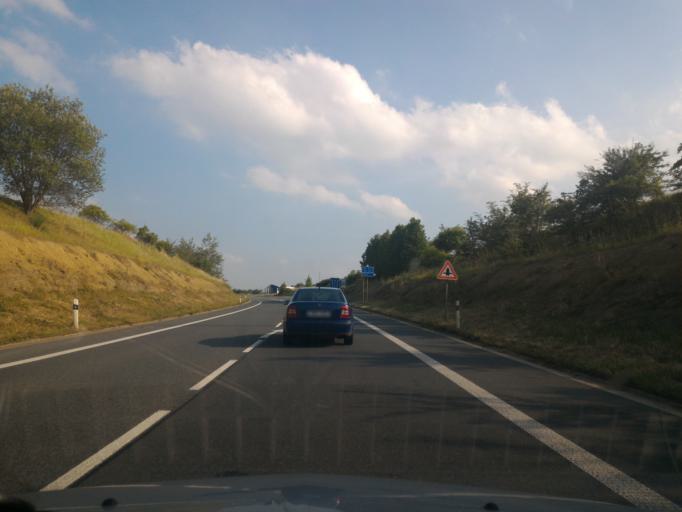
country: CZ
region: Central Bohemia
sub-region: Okres Kutna Hora
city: Caslav
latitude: 49.9013
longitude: 15.4059
